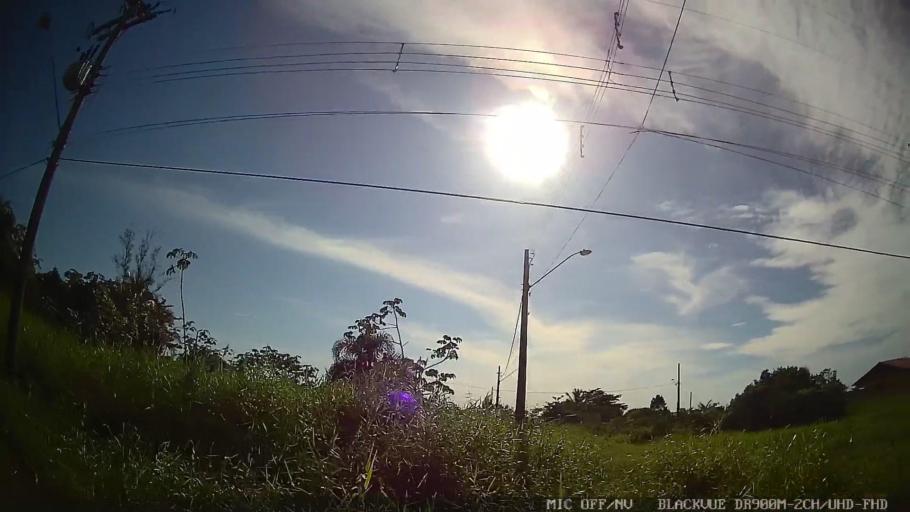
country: BR
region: Sao Paulo
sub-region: Iguape
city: Iguape
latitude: -24.7634
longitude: -47.5827
